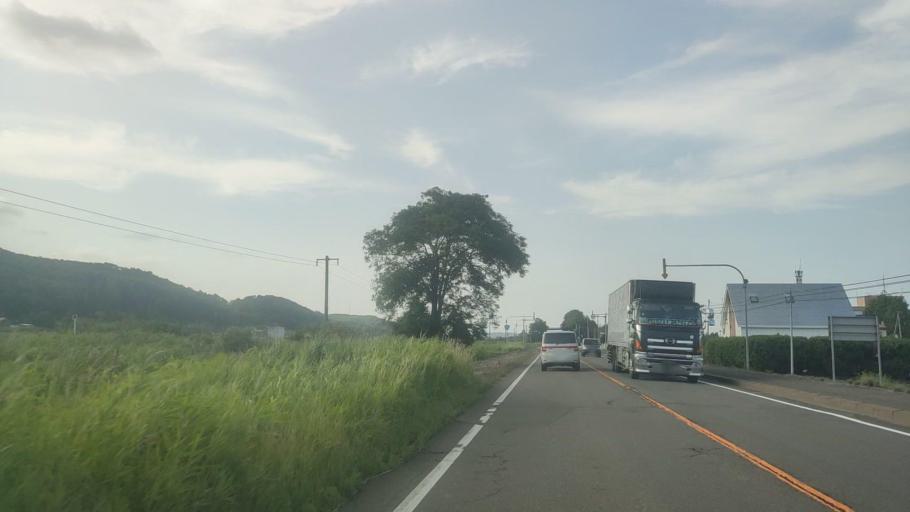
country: JP
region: Hokkaido
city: Iwamizawa
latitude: 42.9971
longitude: 141.7897
